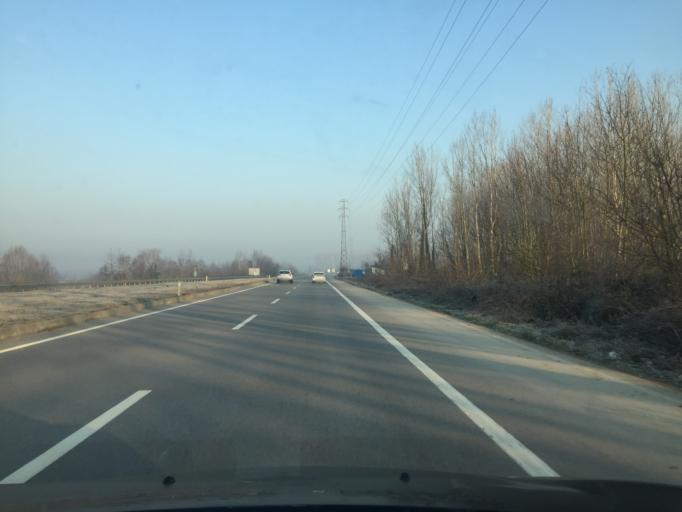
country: TR
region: Sakarya
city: Akyazi
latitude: 40.6884
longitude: 30.5749
